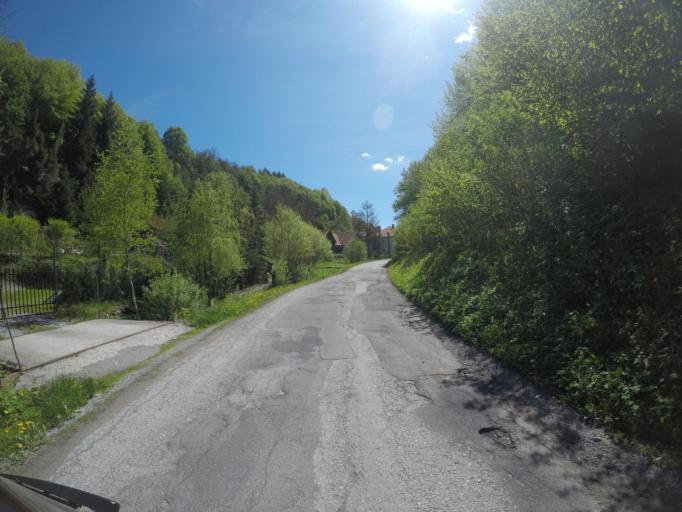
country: SK
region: Banskobystricky
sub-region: Okres Banska Bystrica
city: Banska Bystrica
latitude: 48.7225
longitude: 19.2195
